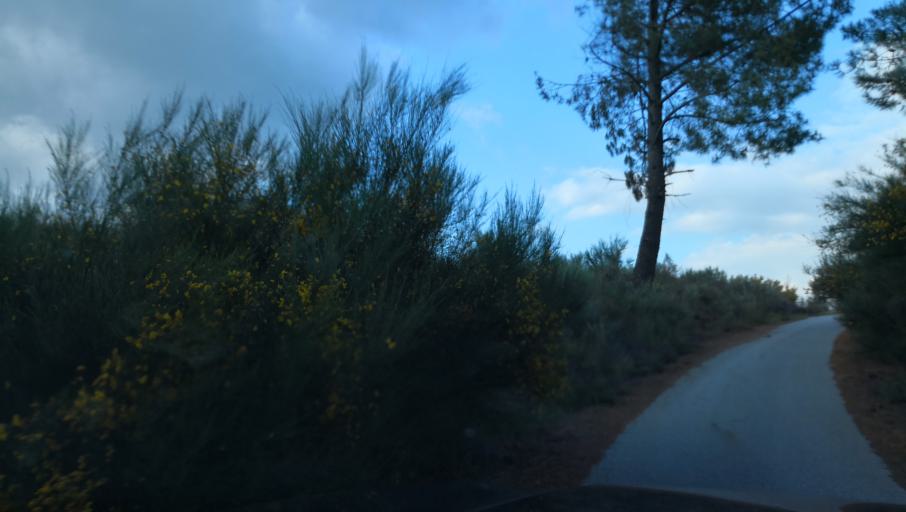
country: PT
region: Vila Real
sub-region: Vila Real
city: Vila Real
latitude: 41.2730
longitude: -7.7877
